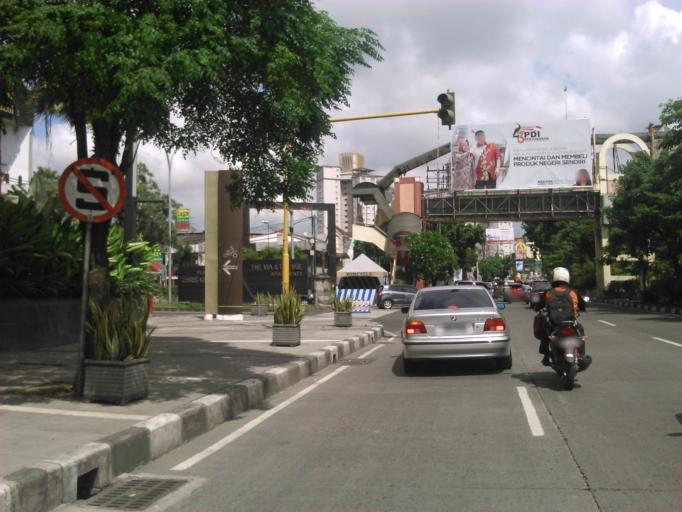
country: ID
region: East Java
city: Jagirsidosermo
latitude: -7.2918
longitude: 112.7189
